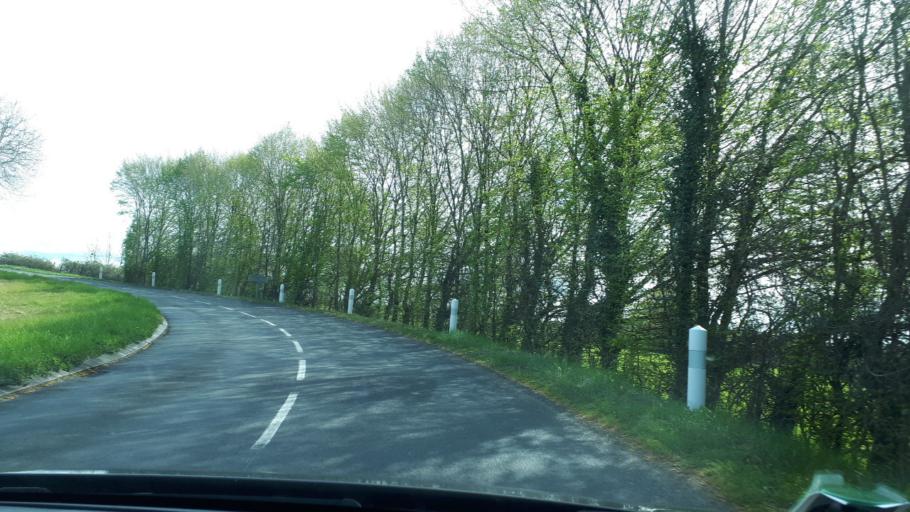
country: FR
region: Pays de la Loire
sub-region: Departement de la Sarthe
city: Yvre-le-Polin
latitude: 47.8214
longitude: 0.1609
